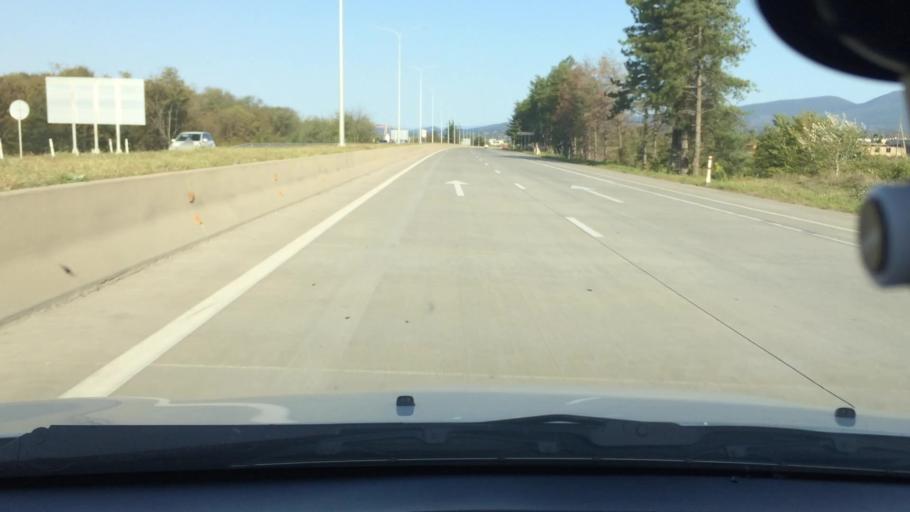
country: GE
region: Imereti
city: Zestap'oni
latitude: 42.1628
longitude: 42.9443
